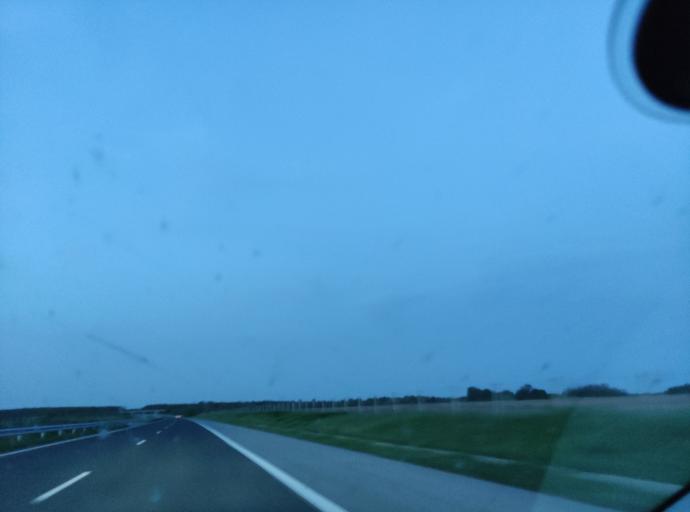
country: BG
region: Stara Zagora
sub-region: Obshtina Stara Zagora
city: Stara Zagora
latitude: 42.3490
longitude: 25.7278
